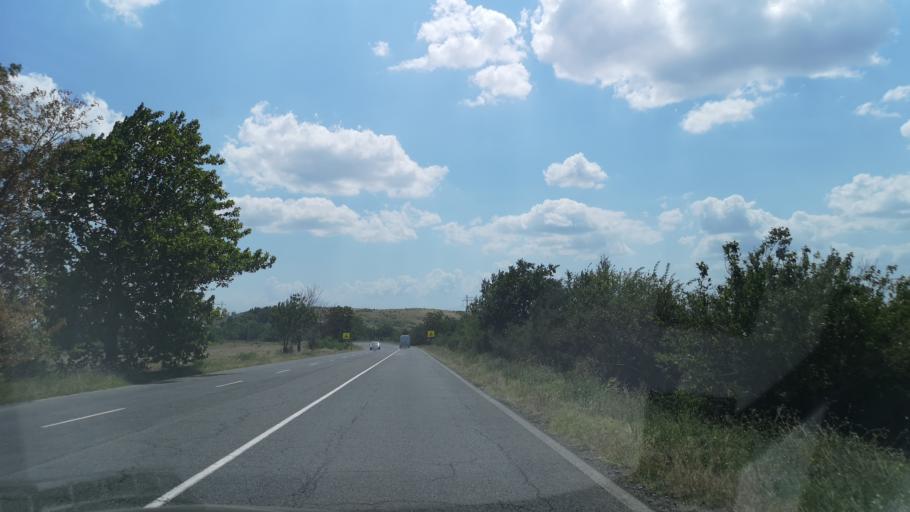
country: BG
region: Burgas
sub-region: Obshtina Kameno
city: Kameno
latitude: 42.6276
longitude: 27.3445
